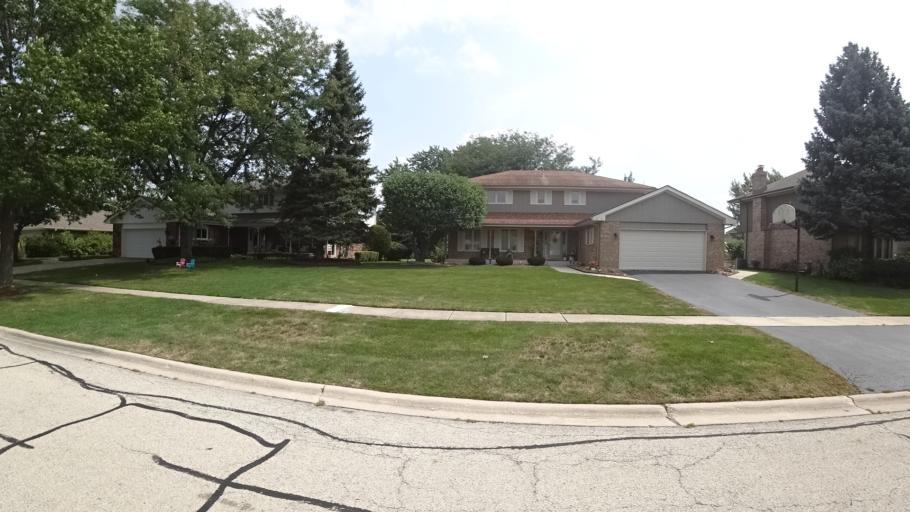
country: US
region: Illinois
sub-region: Will County
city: Goodings Grove
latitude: 41.6216
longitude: -87.9076
